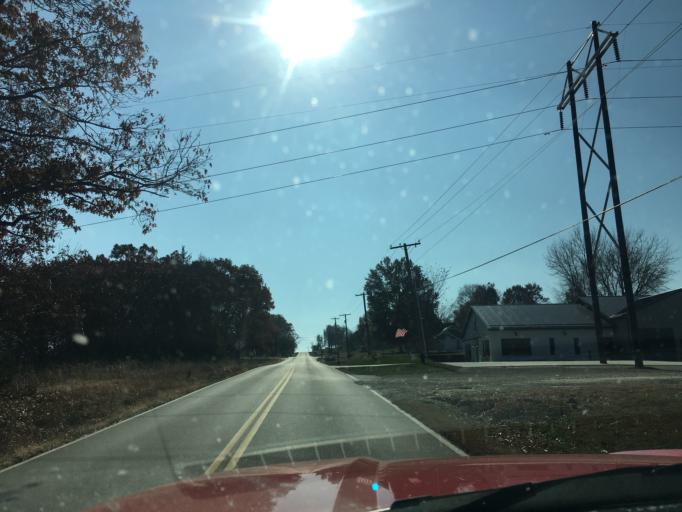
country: US
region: Missouri
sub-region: Cole County
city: Wardsville
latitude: 38.5141
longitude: -92.1762
